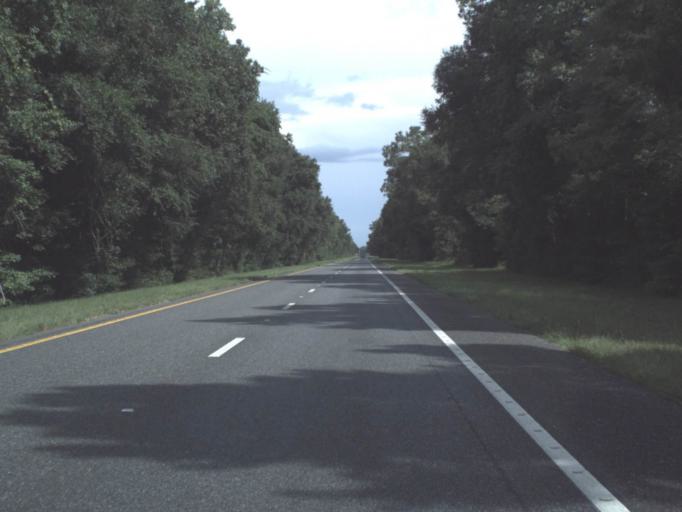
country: US
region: Florida
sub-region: Levy County
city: Bronson
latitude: 29.2689
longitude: -82.7332
